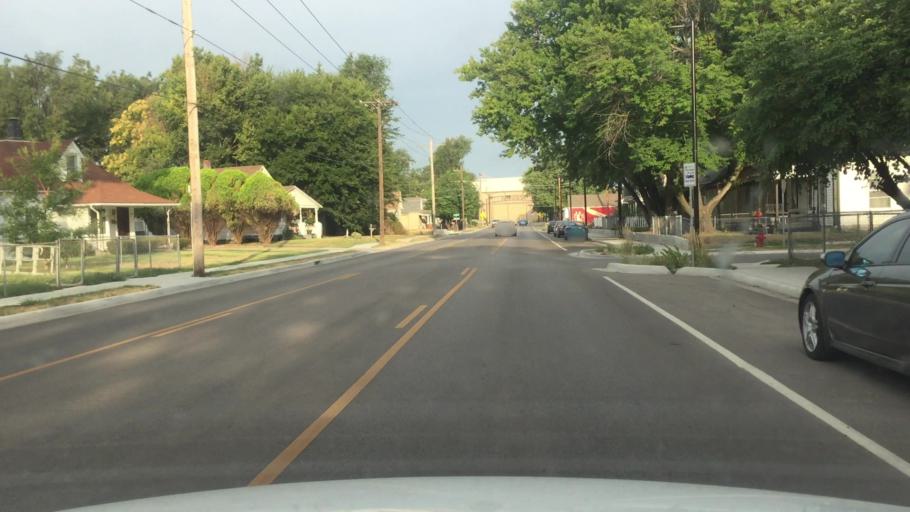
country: US
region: Kansas
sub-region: Shawnee County
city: Topeka
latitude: 39.0589
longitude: -95.6528
